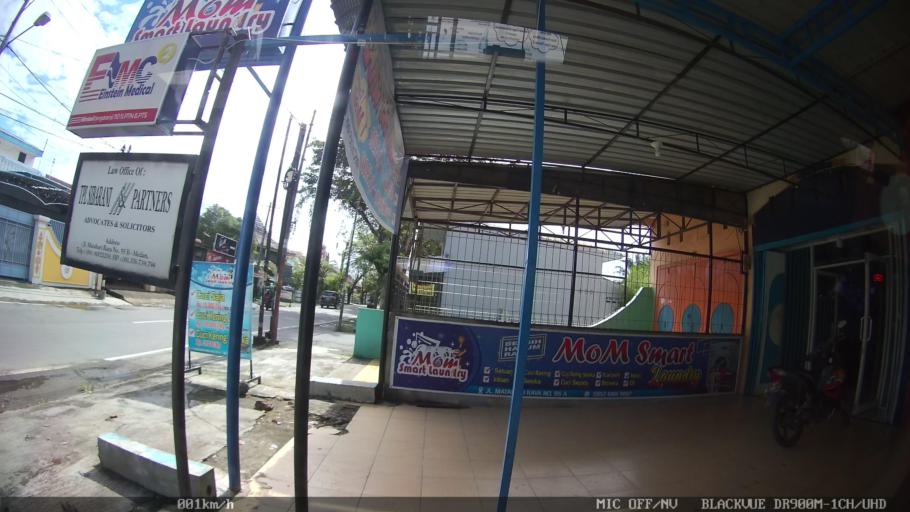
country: ID
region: North Sumatra
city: Sunggal
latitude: 3.6105
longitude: 98.6318
